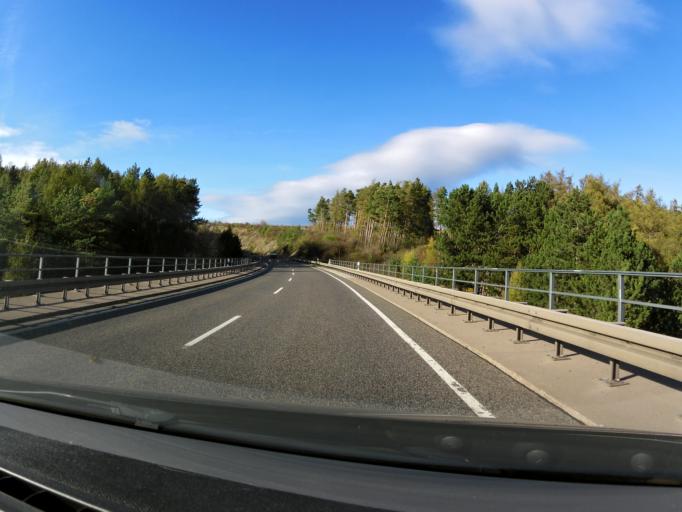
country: DE
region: Thuringia
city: Geschwenda
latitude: 50.7373
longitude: 10.8360
